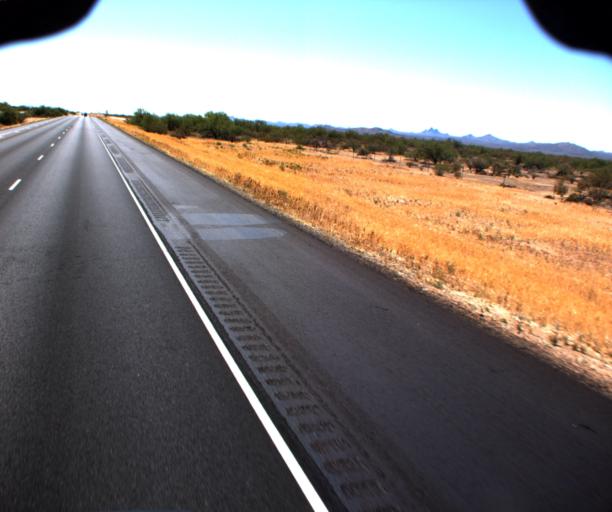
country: US
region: Arizona
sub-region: Yavapai County
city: Congress
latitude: 34.0685
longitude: -112.8722
